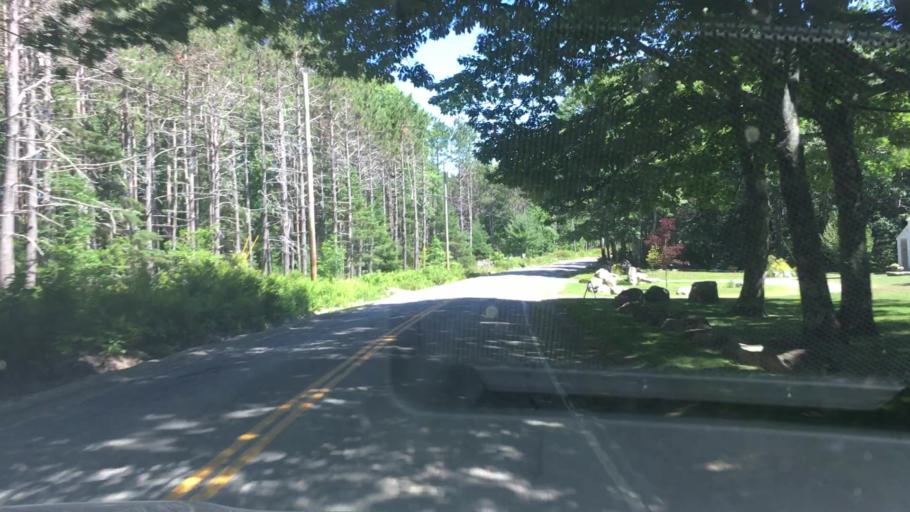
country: US
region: Maine
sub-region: Hancock County
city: Penobscot
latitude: 44.4339
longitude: -68.7140
